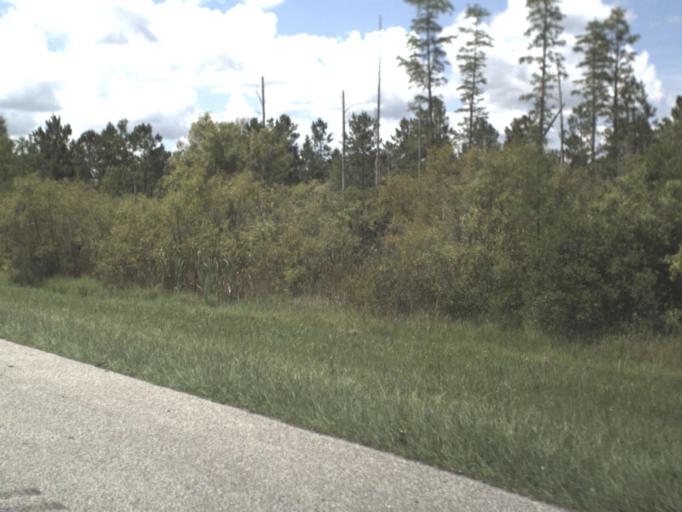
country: US
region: Florida
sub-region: Saint Johns County
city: Saint Augustine Shores
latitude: 29.7396
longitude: -81.3434
